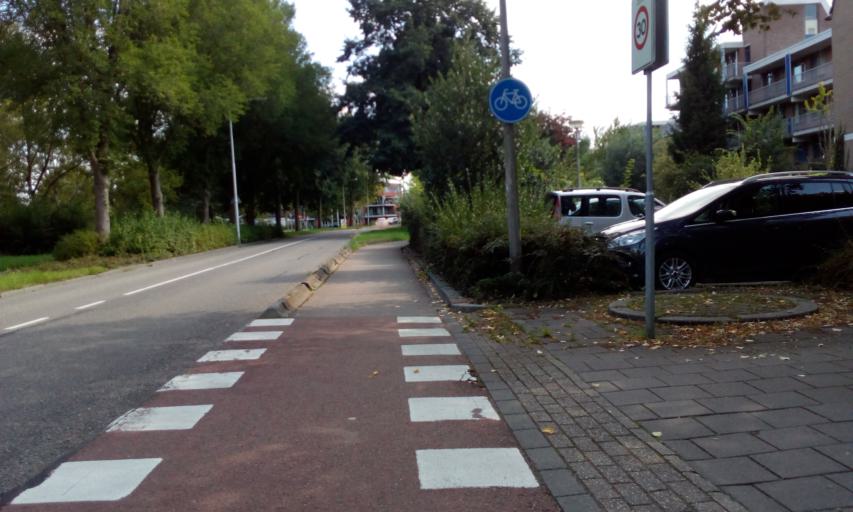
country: NL
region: South Holland
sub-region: Gemeente Gouda
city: Bloemendaal
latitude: 52.0236
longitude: 4.6920
